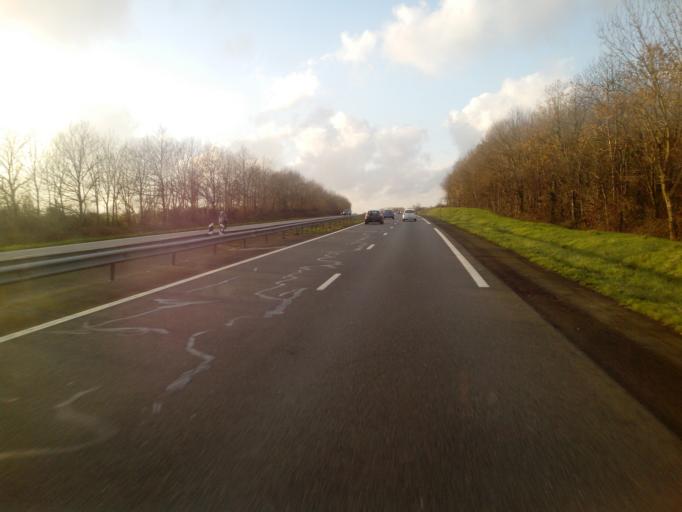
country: FR
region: Pays de la Loire
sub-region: Departement de Maine-et-Loire
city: Saint-Germain-sur-Moine
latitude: 47.1299
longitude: -1.1307
